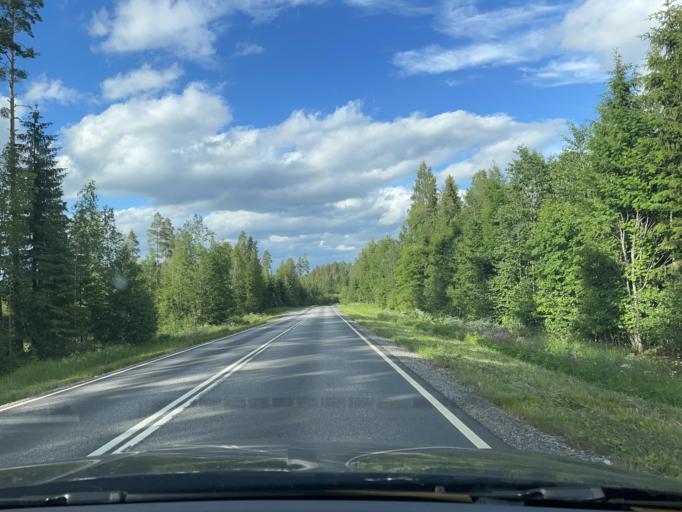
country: FI
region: Central Finland
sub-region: Jaemsae
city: Jaemsaenkoski
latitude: 62.0855
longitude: 25.1459
